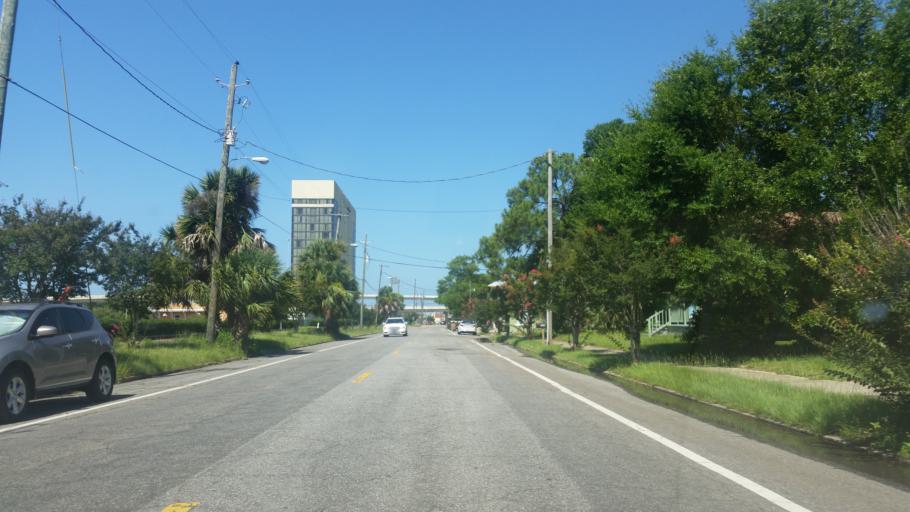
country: US
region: Florida
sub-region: Escambia County
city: Pensacola
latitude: 30.4183
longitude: -87.2076
